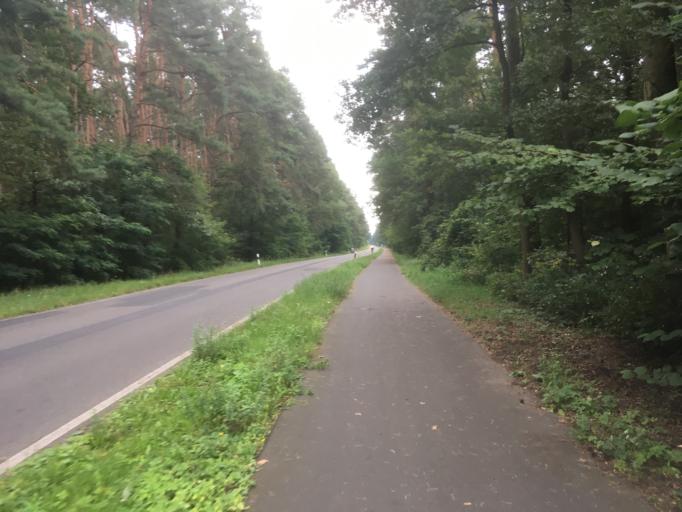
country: DE
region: Brandenburg
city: Erkner
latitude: 52.4061
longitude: 13.7630
